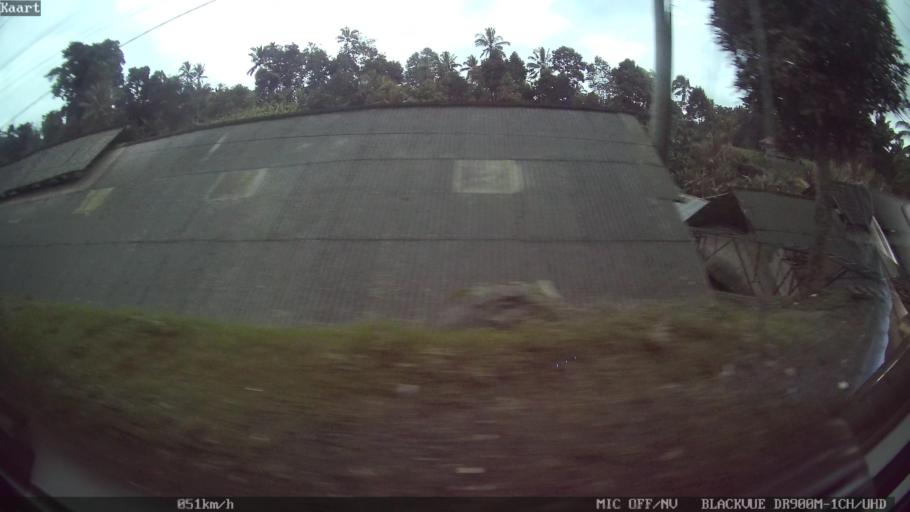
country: ID
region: Bali
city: Empalan
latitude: -8.3891
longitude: 115.1514
